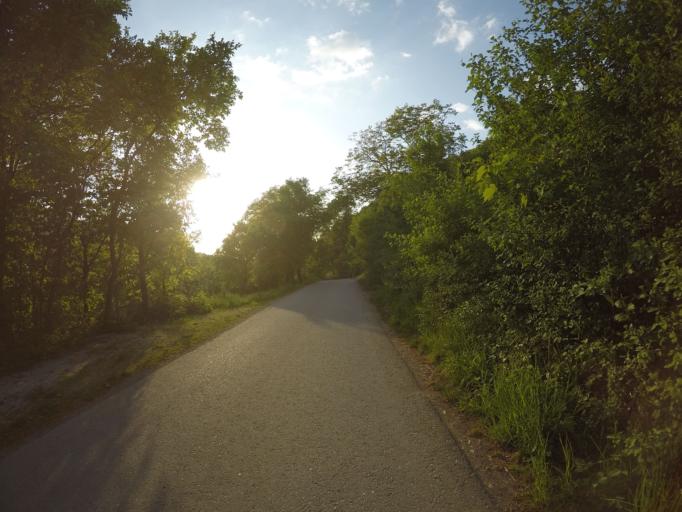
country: DE
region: Baden-Wuerttemberg
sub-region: Tuebingen Region
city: Pfullingen
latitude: 48.4477
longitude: 9.2492
